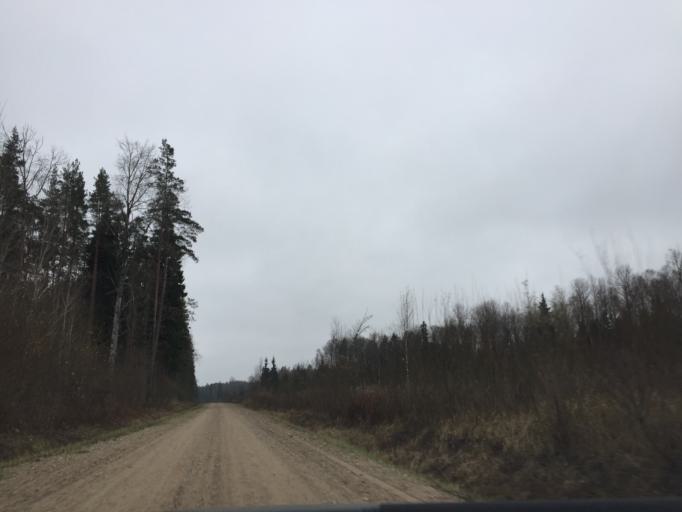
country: LV
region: Limbazu Rajons
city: Limbazi
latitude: 57.4717
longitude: 24.7549
